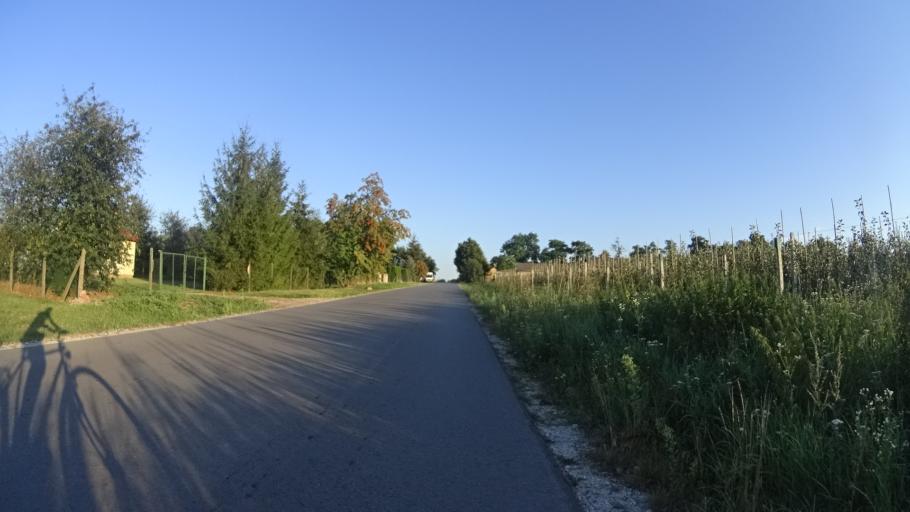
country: PL
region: Masovian Voivodeship
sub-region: Powiat grojecki
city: Goszczyn
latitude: 51.6902
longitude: 20.8180
